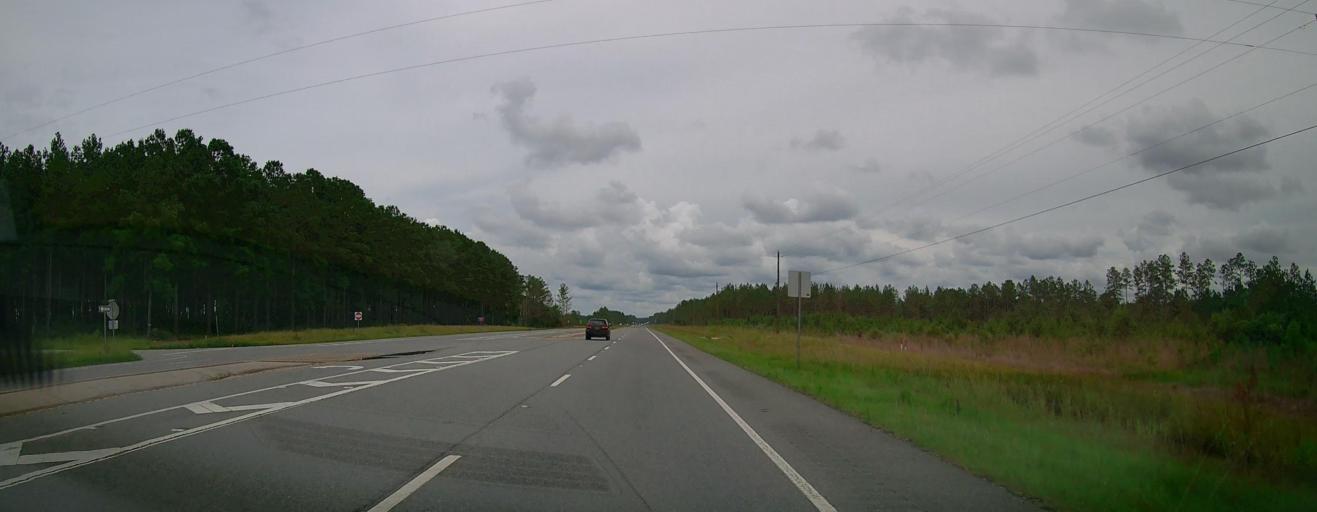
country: US
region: Georgia
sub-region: Appling County
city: Baxley
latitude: 31.7351
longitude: -82.2245
